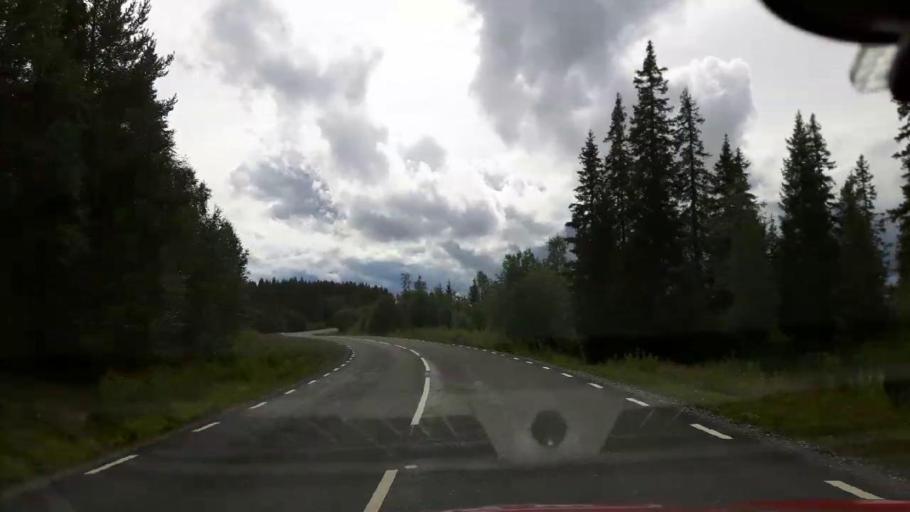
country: NO
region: Nord-Trondelag
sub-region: Lierne
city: Sandvika
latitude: 64.6064
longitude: 14.1197
